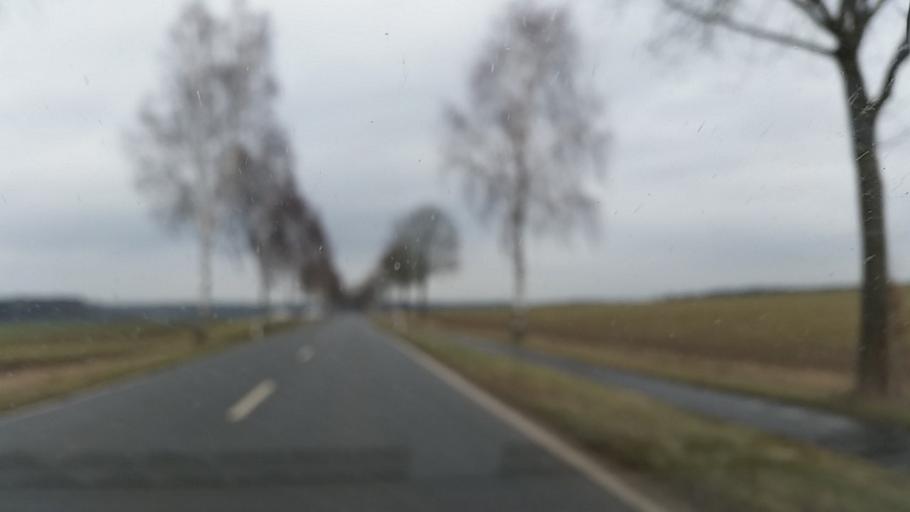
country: DE
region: Lower Saxony
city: Bispingen
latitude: 53.1130
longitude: 10.0010
